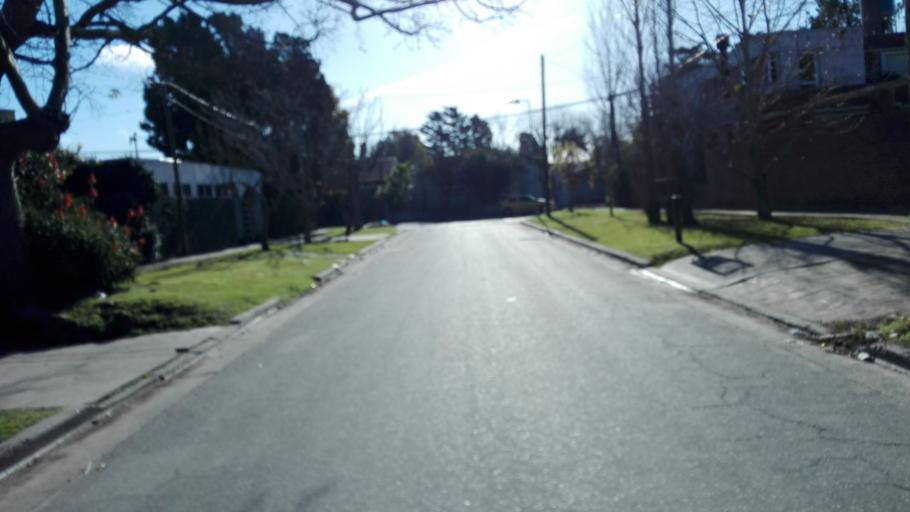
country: AR
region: Buenos Aires
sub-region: Partido de La Plata
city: La Plata
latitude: -34.8801
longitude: -58.0077
